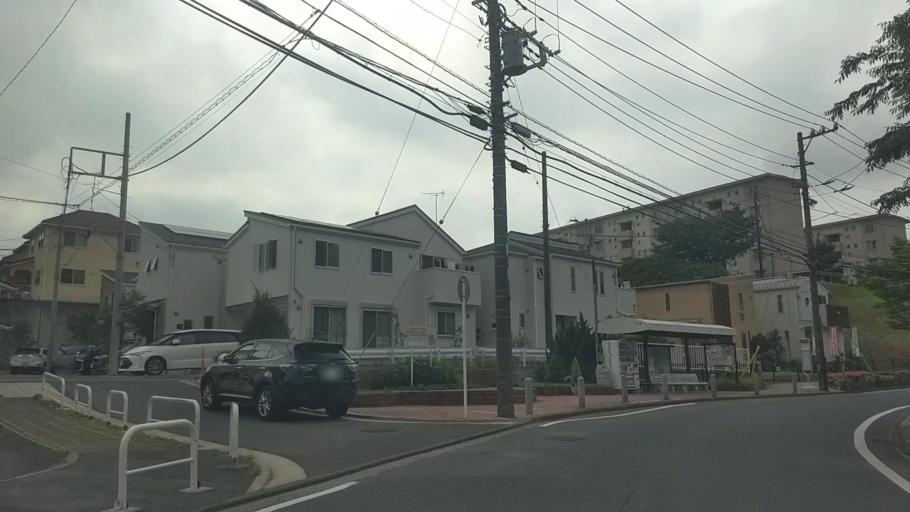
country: JP
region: Kanagawa
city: Kamakura
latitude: 35.3738
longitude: 139.5365
